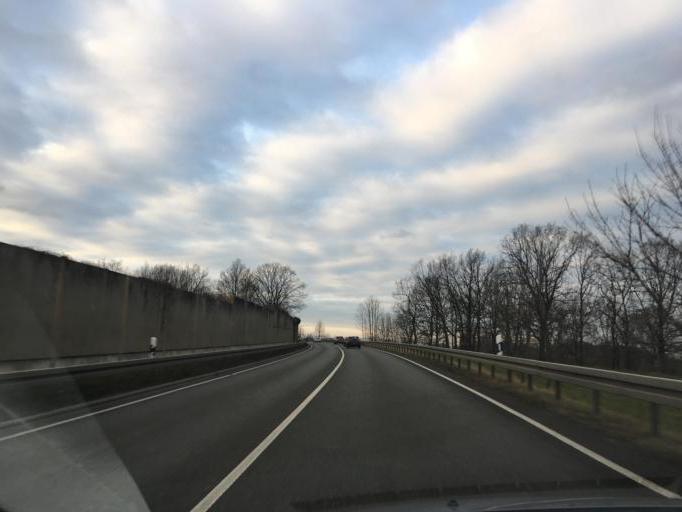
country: DE
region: Thuringia
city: Nobitz
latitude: 51.0018
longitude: 12.4689
